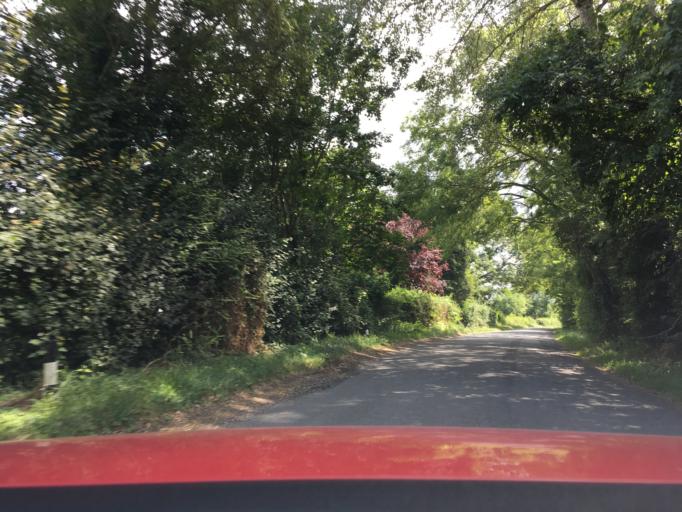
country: GB
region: England
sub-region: Gloucestershire
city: Gloucester
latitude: 51.9094
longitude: -2.2314
